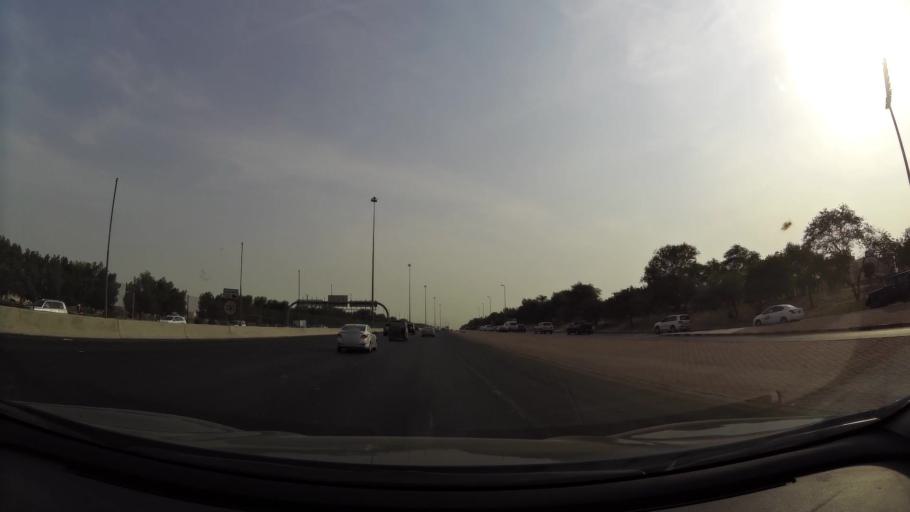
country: KW
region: Al Farwaniyah
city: Janub as Surrah
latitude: 29.2823
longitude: 47.9856
